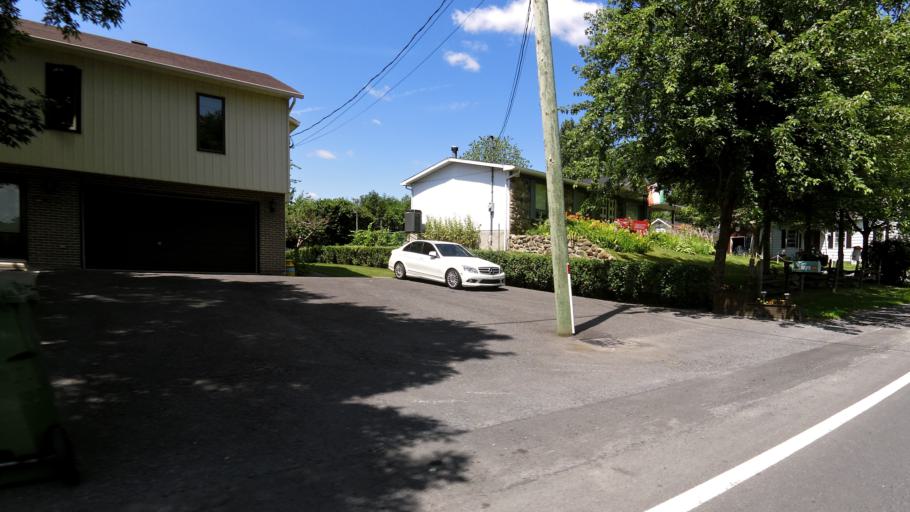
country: CA
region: Quebec
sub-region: Monteregie
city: Richelieu
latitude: 45.3877
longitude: -73.2502
